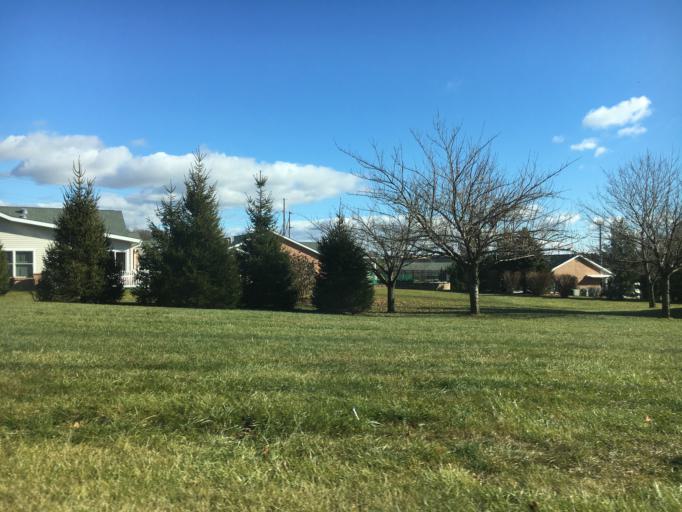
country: US
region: Pennsylvania
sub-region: Lehigh County
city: Stiles
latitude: 40.6406
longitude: -75.5130
